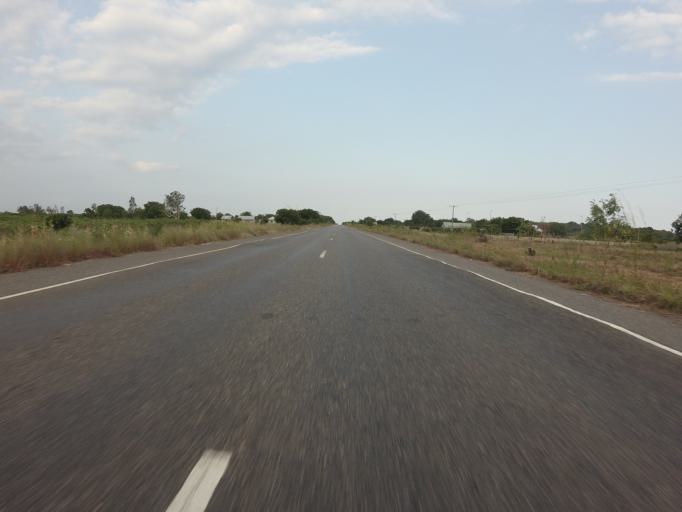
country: GH
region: Volta
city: Anloga
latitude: 6.0882
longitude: 0.5398
